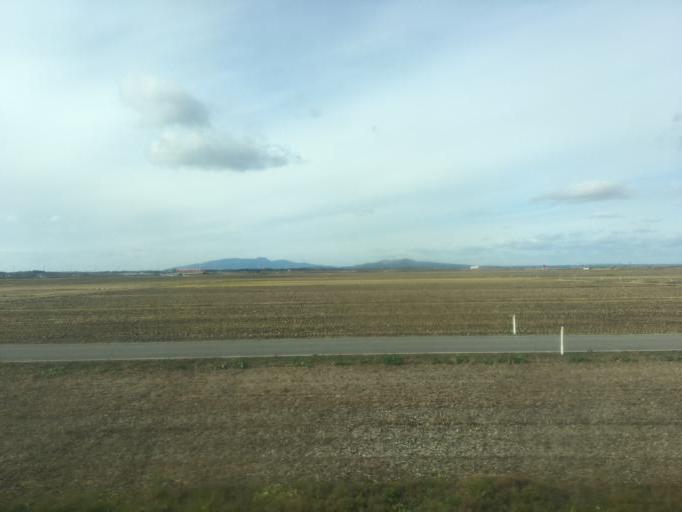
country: JP
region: Akita
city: Tenno
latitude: 39.8744
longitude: 140.0642
